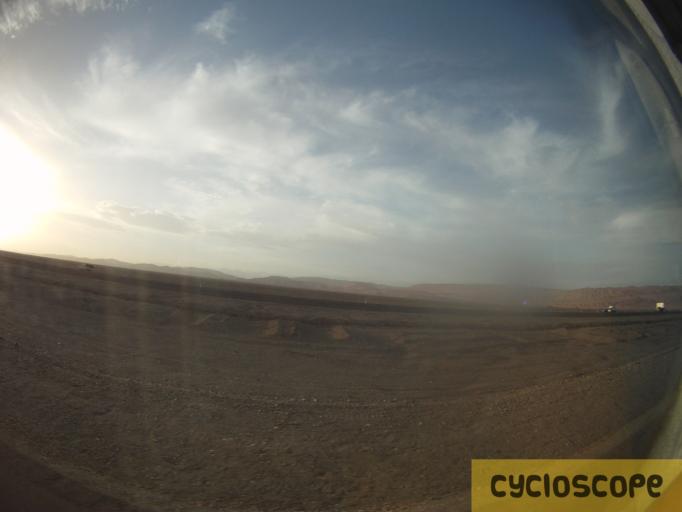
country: CN
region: Xinjiang Uygur Zizhiqu
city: Laochenglu
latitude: 42.9216
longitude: 89.4414
